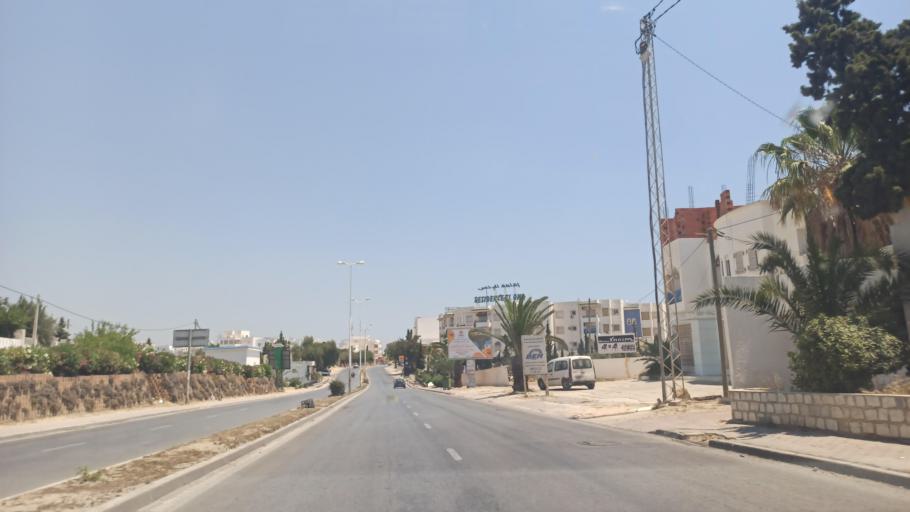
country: TN
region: Nabul
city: Al Hammamat
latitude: 36.4086
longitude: 10.6396
